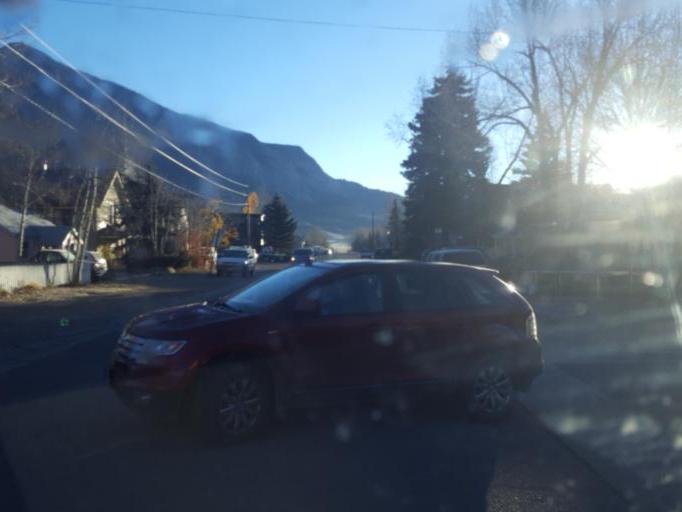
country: US
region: Colorado
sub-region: Gunnison County
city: Crested Butte
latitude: 38.8688
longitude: -106.9827
